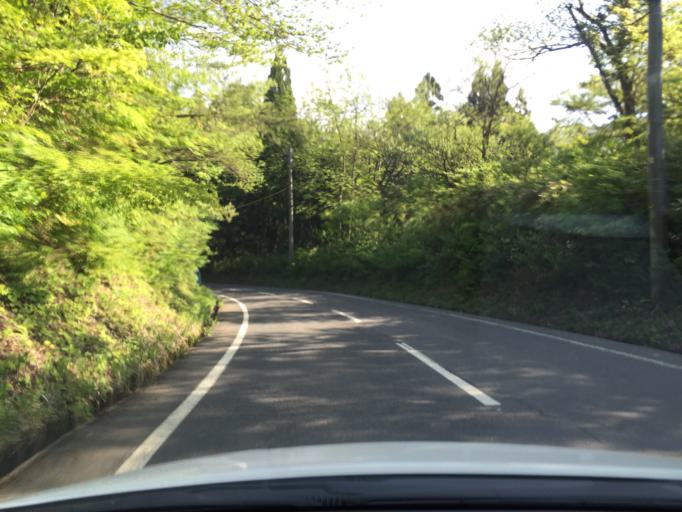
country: JP
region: Fukushima
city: Kitakata
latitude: 37.6917
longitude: 139.5801
